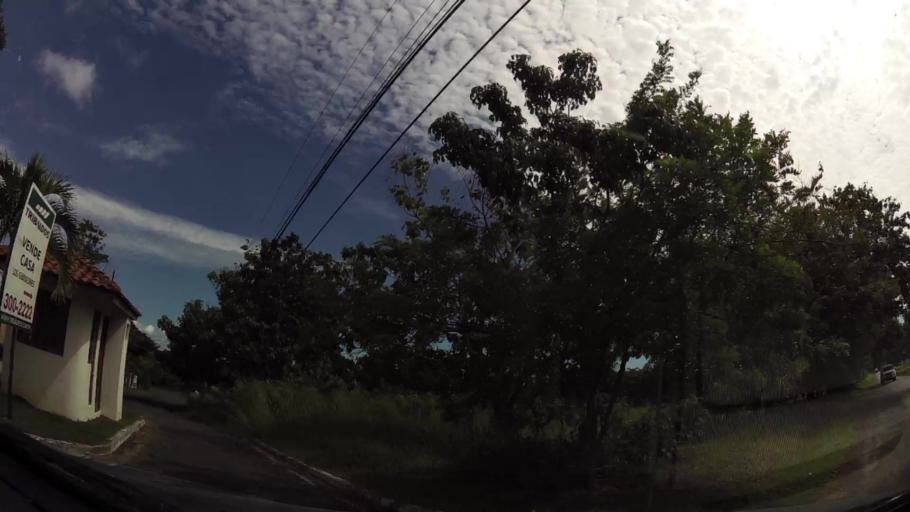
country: PA
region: Panama
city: Nueva Gorgona
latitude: 8.5350
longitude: -79.8974
